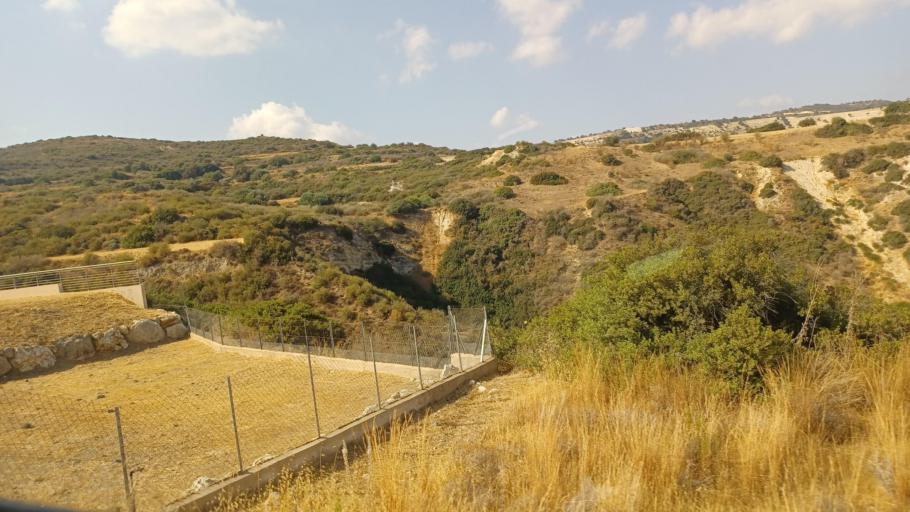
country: CY
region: Pafos
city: Polis
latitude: 34.9930
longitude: 32.4330
